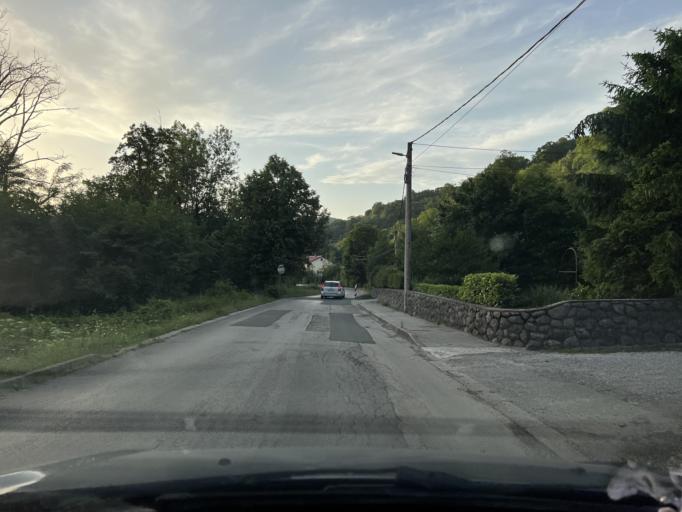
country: HR
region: Primorsko-Goranska
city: Drazice
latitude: 45.3900
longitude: 14.4392
